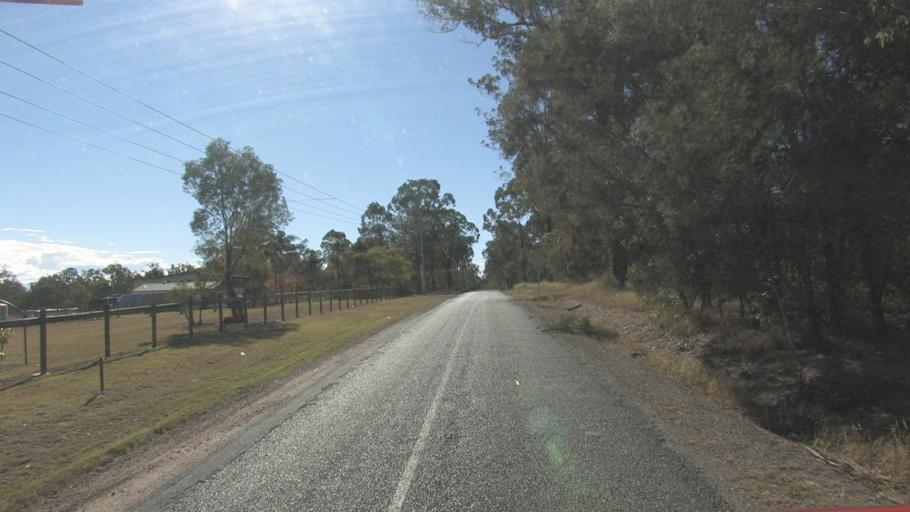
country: AU
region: Queensland
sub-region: Logan
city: Chambers Flat
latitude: -27.7964
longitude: 153.0705
